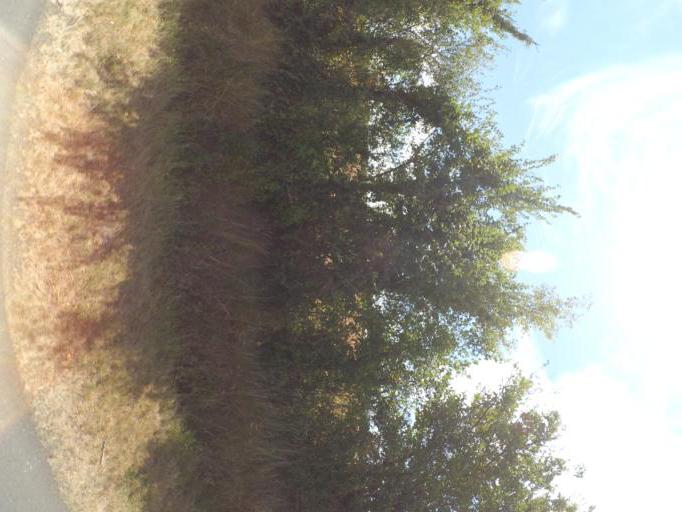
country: FR
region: Poitou-Charentes
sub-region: Departement de la Vienne
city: Saint-Maurice-la-Clouere
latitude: 46.3976
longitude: 0.3570
